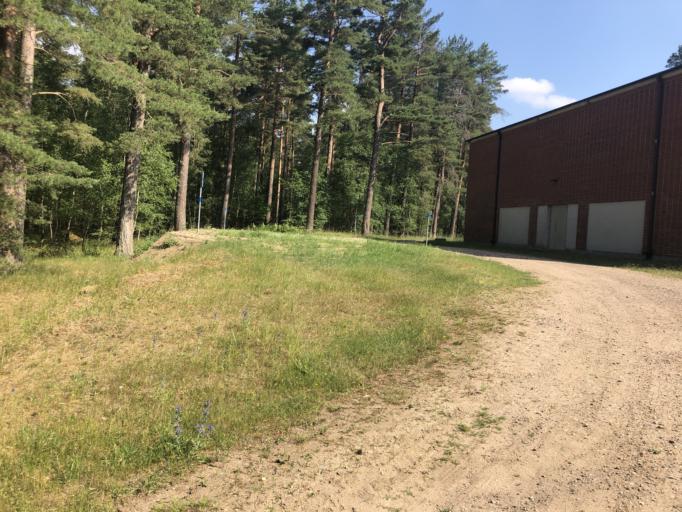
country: SE
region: Skane
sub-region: Lunds Kommun
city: Veberod
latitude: 55.6607
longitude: 13.5589
